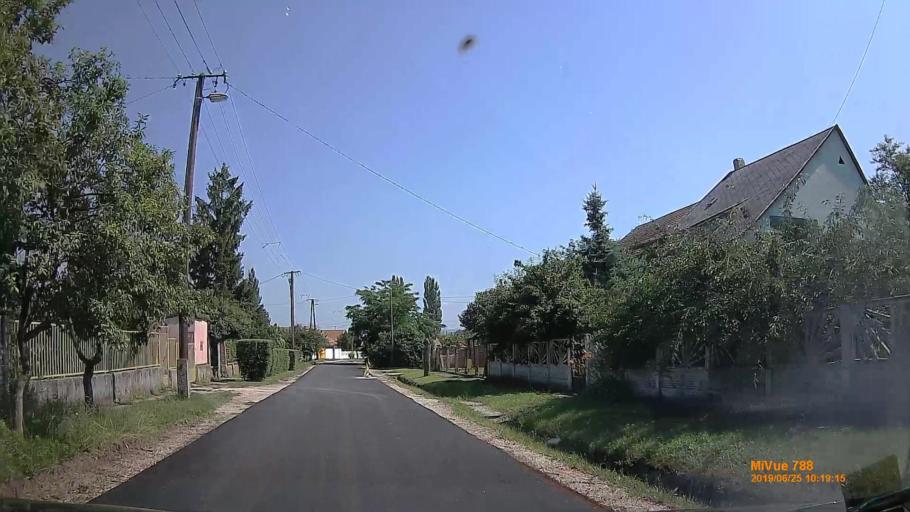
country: HU
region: Komarom-Esztergom
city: Tokod
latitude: 47.7353
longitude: 18.6956
